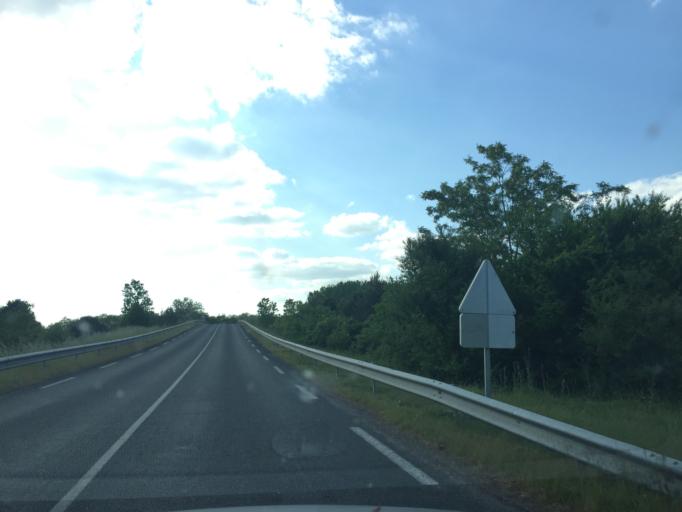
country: FR
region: Aquitaine
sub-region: Departement de la Gironde
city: Saint-Denis-de-Pile
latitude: 44.9719
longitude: -0.1920
